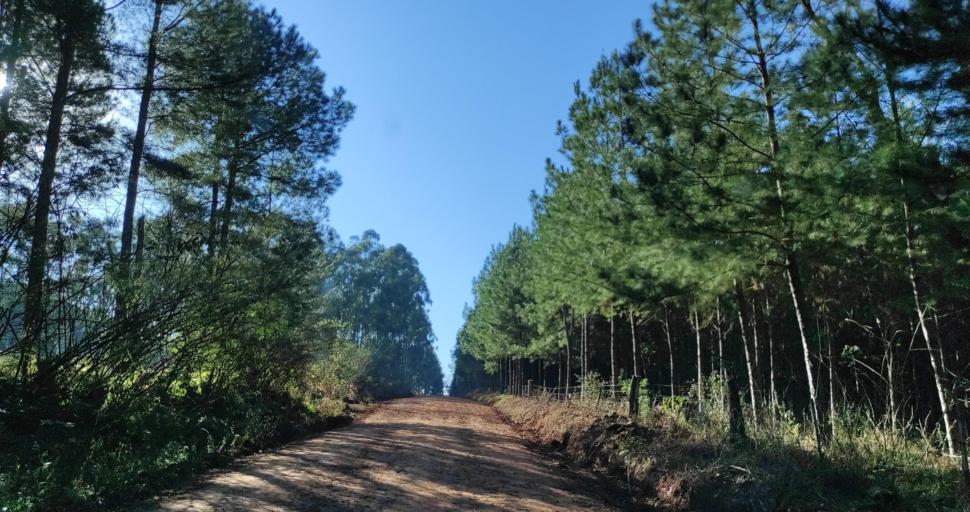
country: AR
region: Misiones
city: Capiovi
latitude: -26.8801
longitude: -55.0262
